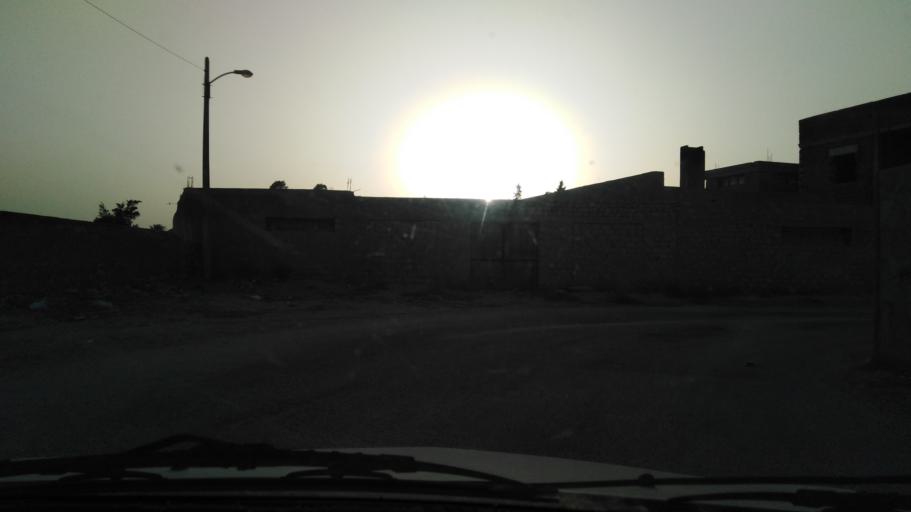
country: TN
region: Qabis
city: Gabes
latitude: 33.9570
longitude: 10.0025
